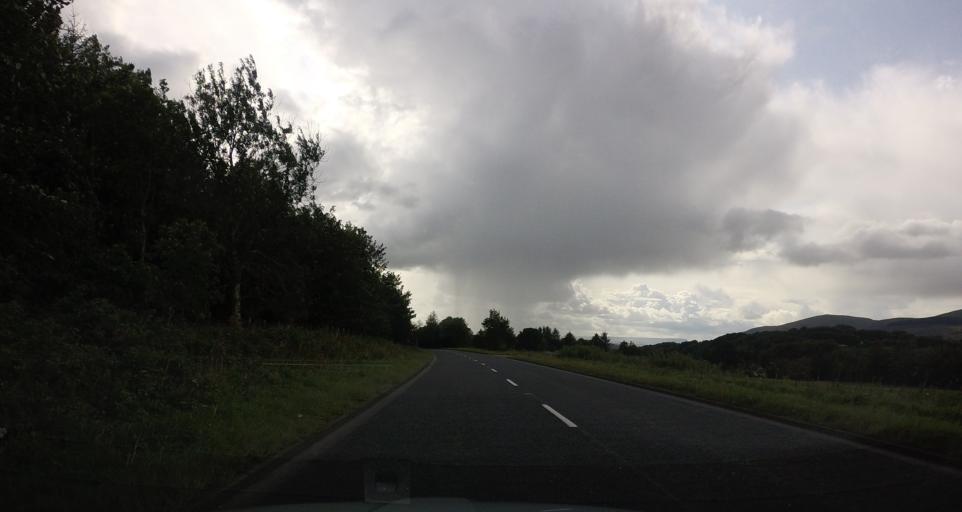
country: GB
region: Scotland
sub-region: Fife
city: Saline
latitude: 56.1780
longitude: -3.5769
